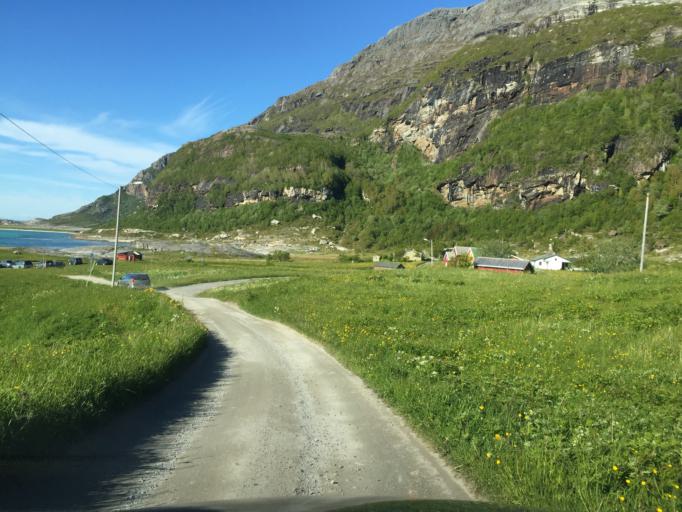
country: NO
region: Nordland
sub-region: Bodo
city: Loding
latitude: 67.4101
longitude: 14.6282
